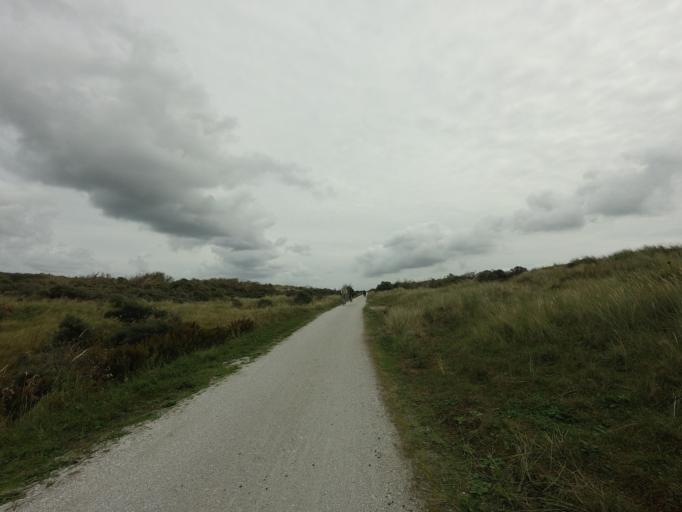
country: NL
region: Friesland
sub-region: Gemeente Ameland
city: Hollum
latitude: 53.4582
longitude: 5.6787
